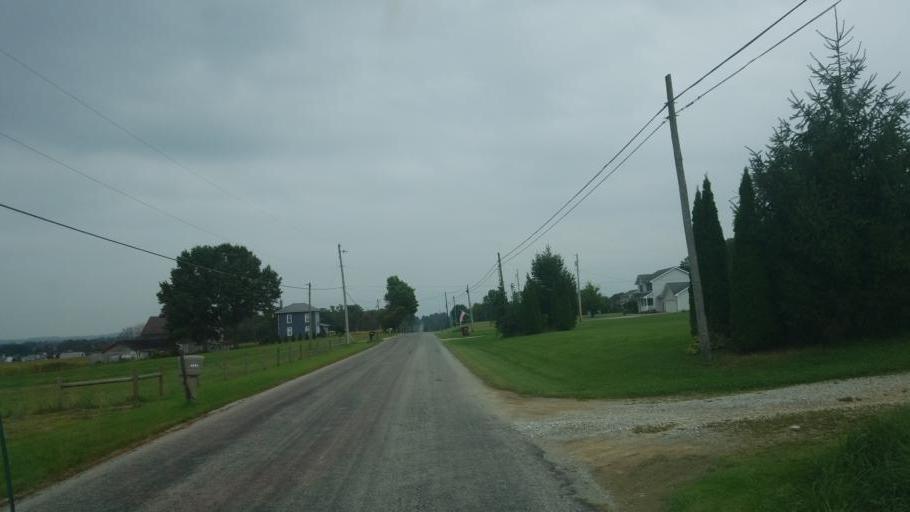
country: US
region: Ohio
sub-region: Wayne County
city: Creston
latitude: 40.9598
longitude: -81.9222
